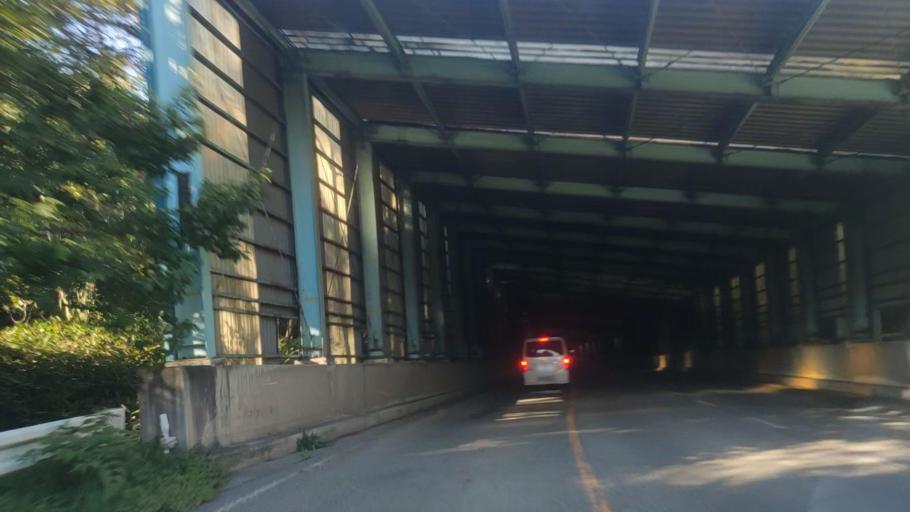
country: JP
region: Nagano
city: Kamimaruko
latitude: 36.1768
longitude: 138.2815
